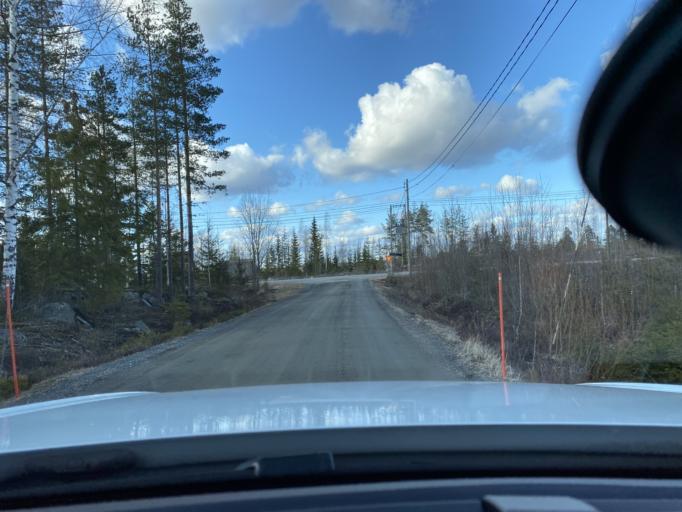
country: FI
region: Pirkanmaa
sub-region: Lounais-Pirkanmaa
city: Punkalaidun
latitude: 61.0944
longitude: 23.1362
